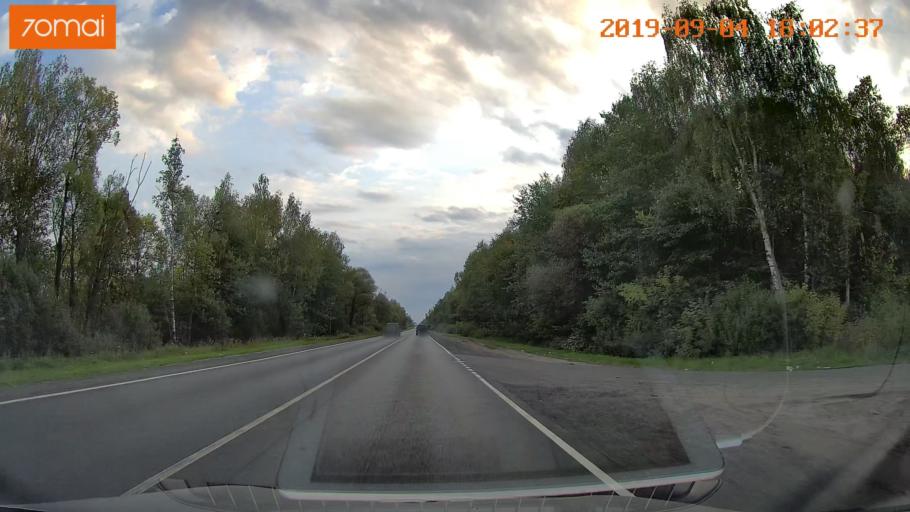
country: RU
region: Moskovskaya
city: Il'inskiy Pogost
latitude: 55.4723
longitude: 38.8625
